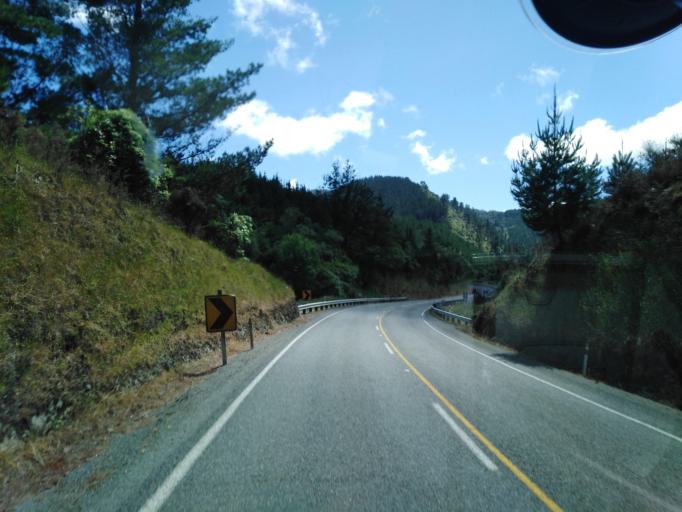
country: NZ
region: Nelson
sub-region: Nelson City
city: Nelson
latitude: -41.1769
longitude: 173.5610
